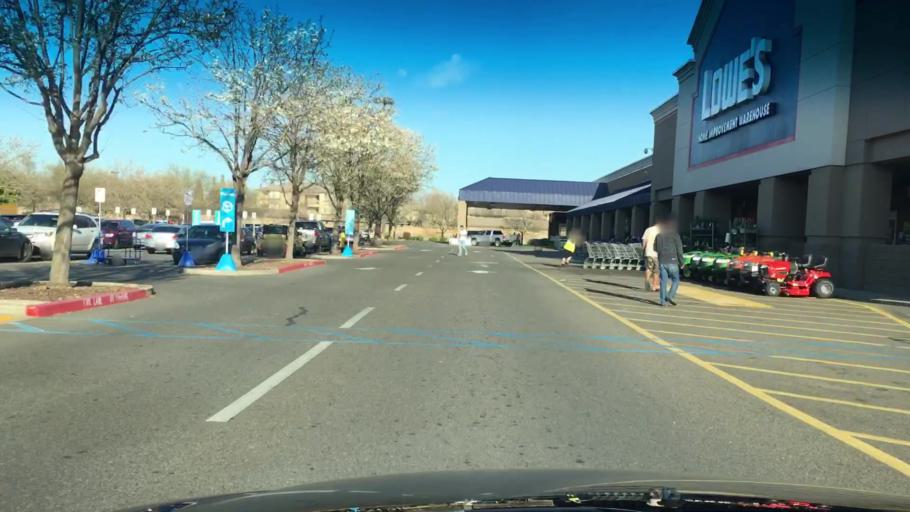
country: US
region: California
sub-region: Sacramento County
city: Laguna
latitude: 38.4540
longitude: -121.4044
